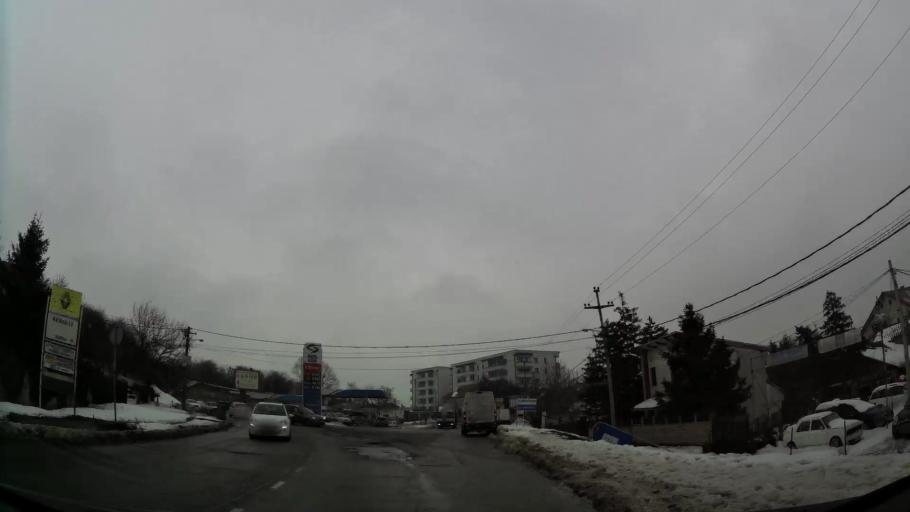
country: RS
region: Central Serbia
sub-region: Belgrade
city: Zvezdara
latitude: 44.7751
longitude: 20.5353
